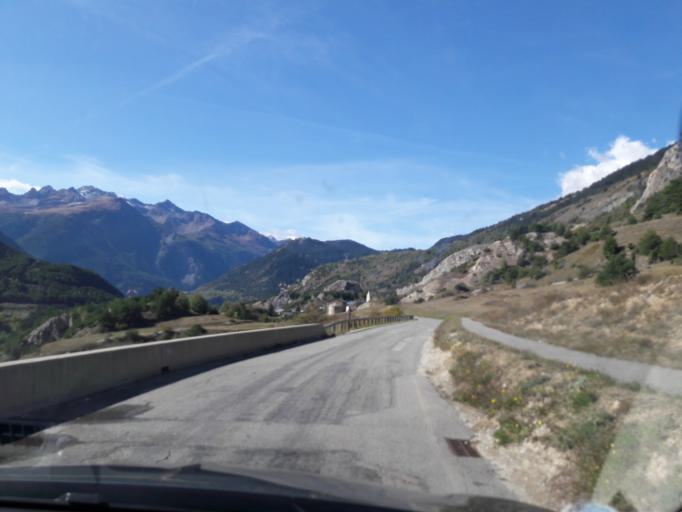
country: FR
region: Rhone-Alpes
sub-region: Departement de la Savoie
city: Modane
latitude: 45.2150
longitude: 6.7080
